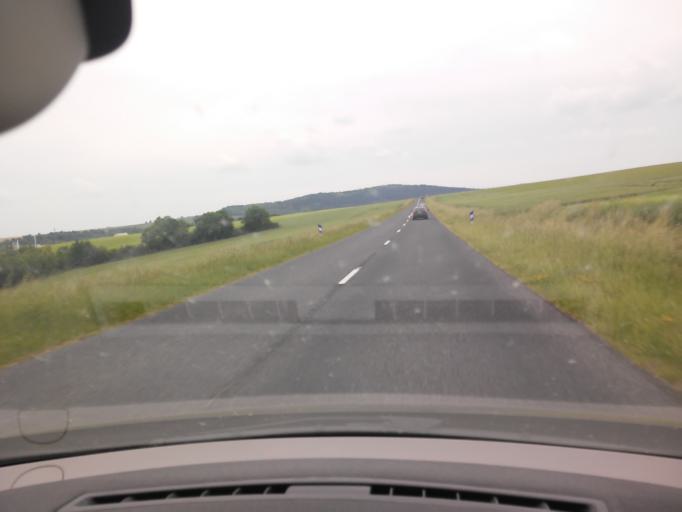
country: FR
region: Lorraine
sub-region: Departement de la Meuse
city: Saint-Mihiel
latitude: 48.8524
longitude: 5.5175
